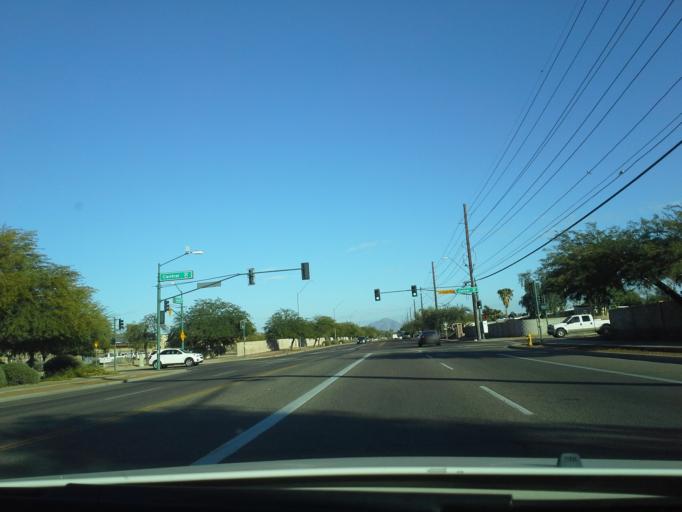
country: US
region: Arizona
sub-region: Maricopa County
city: Glendale
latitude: 33.6547
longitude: -112.0749
